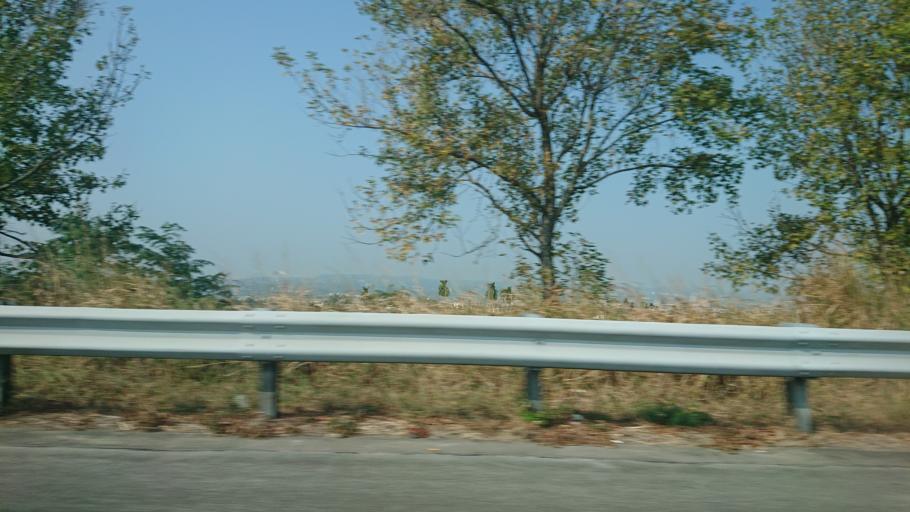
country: TW
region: Taiwan
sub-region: Nantou
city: Nantou
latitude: 23.8888
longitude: 120.7100
